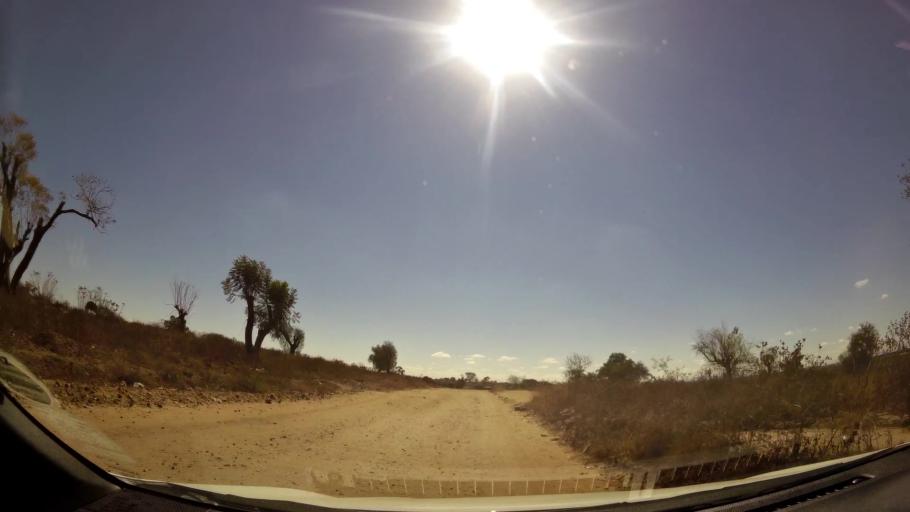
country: ZA
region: Limpopo
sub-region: Capricorn District Municipality
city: Polokwane
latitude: -23.8799
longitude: 29.4251
